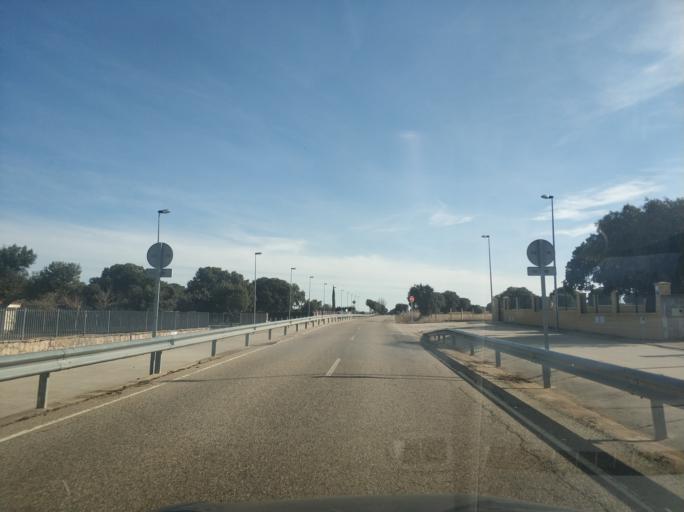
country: ES
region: Castille and Leon
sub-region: Provincia de Salamanca
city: Florida de Liebana
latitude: 41.0180
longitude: -5.7445
